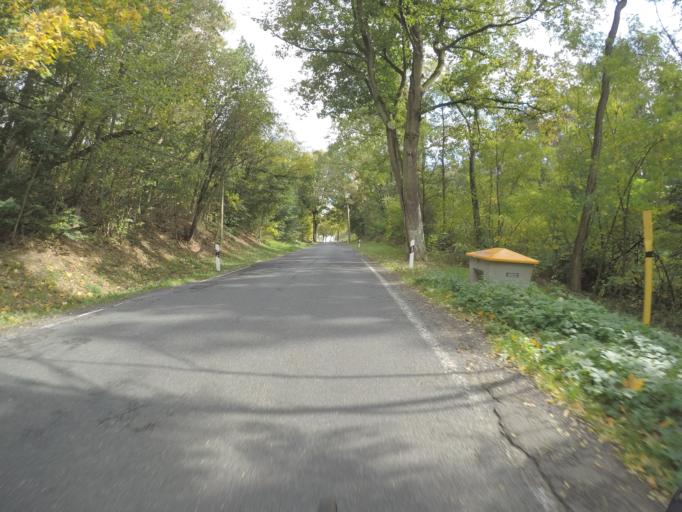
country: DE
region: Brandenburg
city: Strausberg
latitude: 52.6030
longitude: 13.8364
